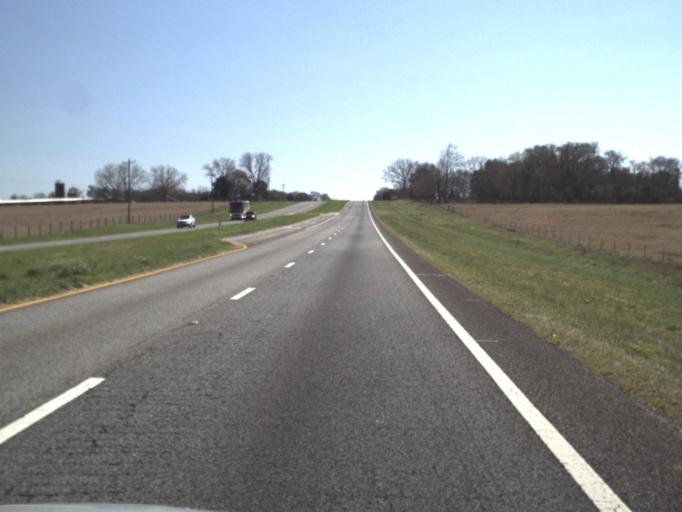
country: US
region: Florida
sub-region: Jackson County
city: Graceville
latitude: 30.8999
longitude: -85.3735
